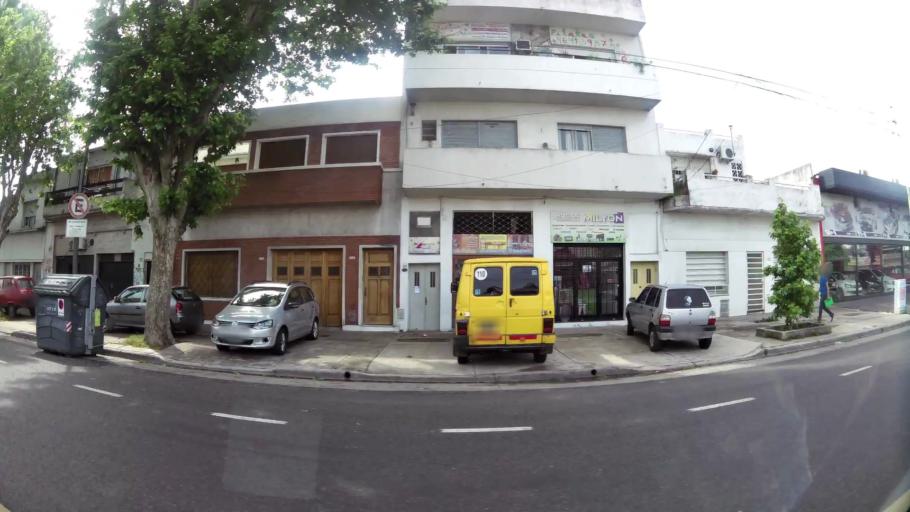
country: AR
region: Buenos Aires F.D.
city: Villa Santa Rita
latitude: -34.6465
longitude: -58.5037
